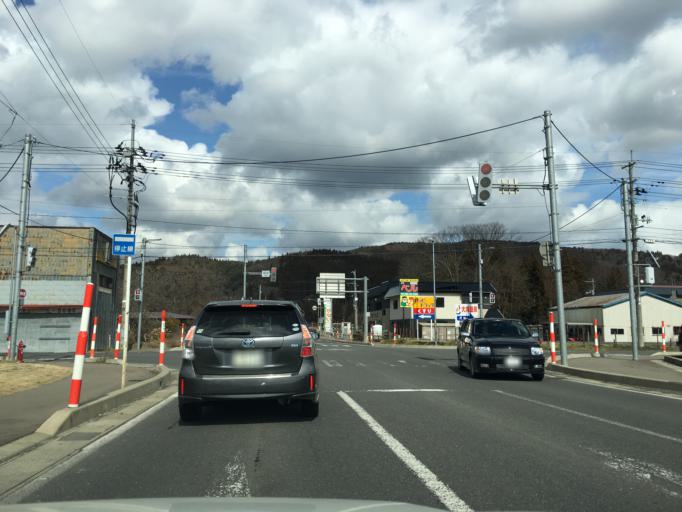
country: JP
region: Akita
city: Odate
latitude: 40.2255
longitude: 140.5897
